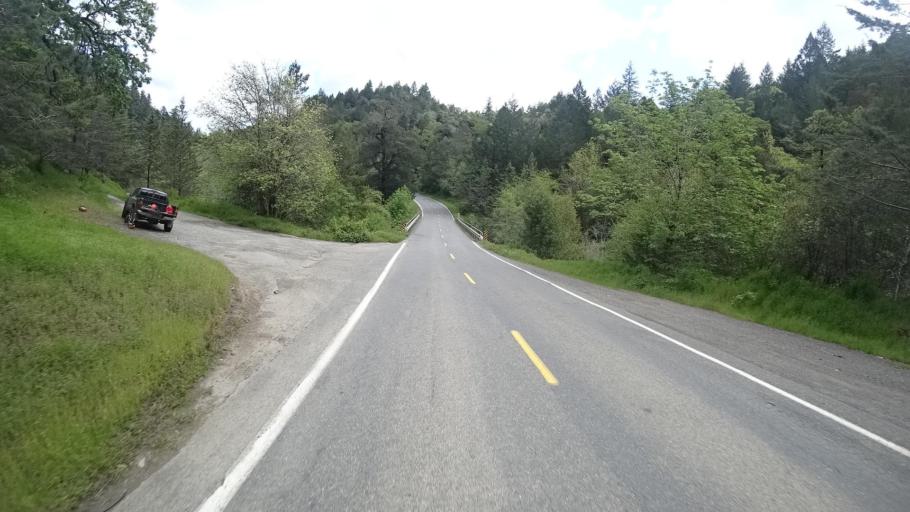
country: US
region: California
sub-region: Humboldt County
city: Redway
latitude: 40.1261
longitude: -123.8686
